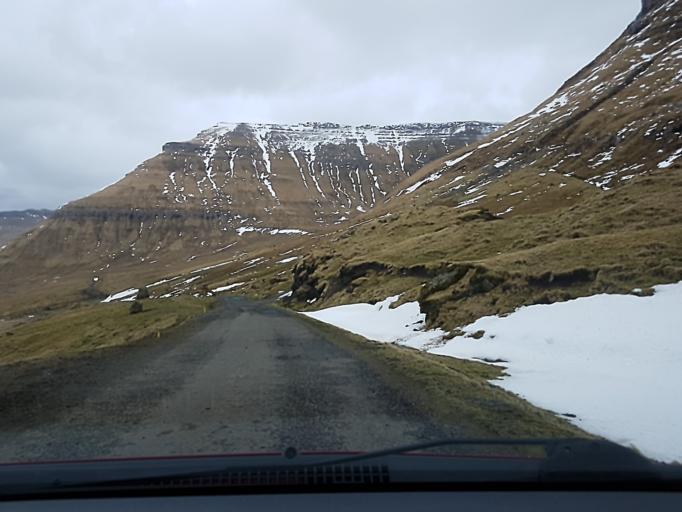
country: FO
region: Streymoy
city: Kollafjordhur
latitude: 62.0183
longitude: -6.9067
